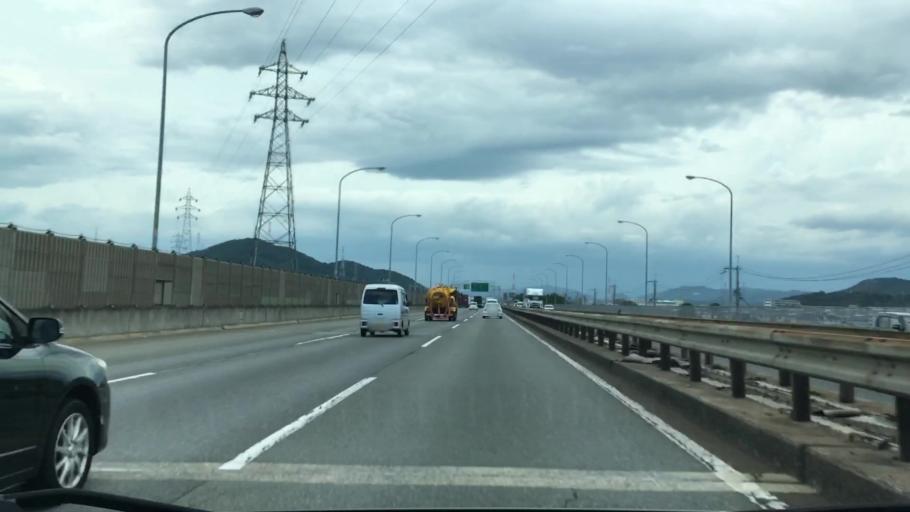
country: JP
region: Hyogo
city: Shirahamacho-usazakiminami
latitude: 34.7938
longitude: 134.7648
